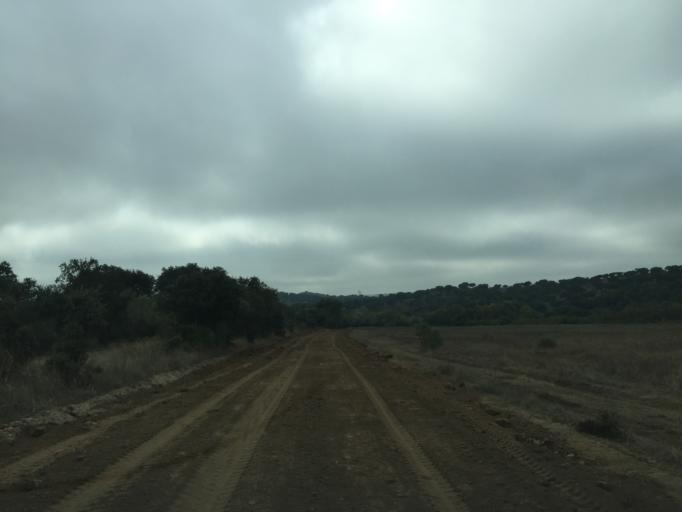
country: PT
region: Portalegre
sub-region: Fronteira
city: Fronteira
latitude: 39.0697
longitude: -7.6150
